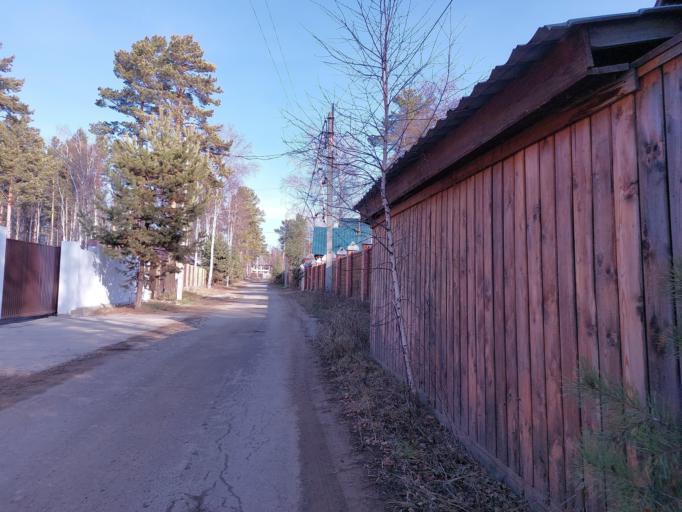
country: RU
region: Irkutsk
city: Pivovarikha
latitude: 52.1879
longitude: 104.4550
